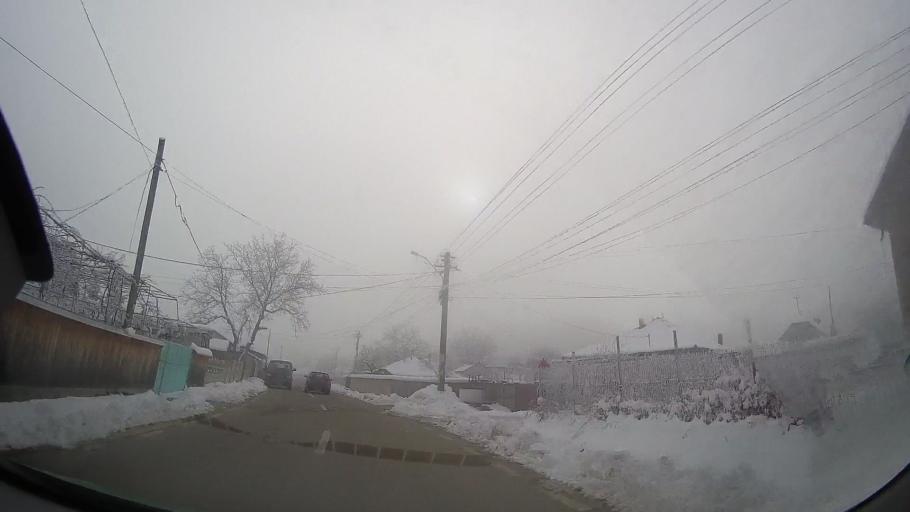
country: RO
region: Iasi
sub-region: Comuna Valea Seaca
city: Valea Seaca
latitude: 47.2892
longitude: 26.6667
